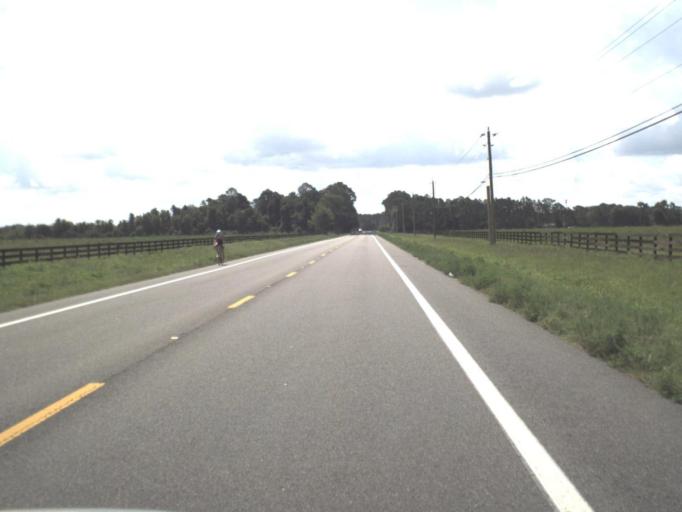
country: US
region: Florida
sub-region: Clay County
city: Green Cove Springs
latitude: 29.9799
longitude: -81.5534
